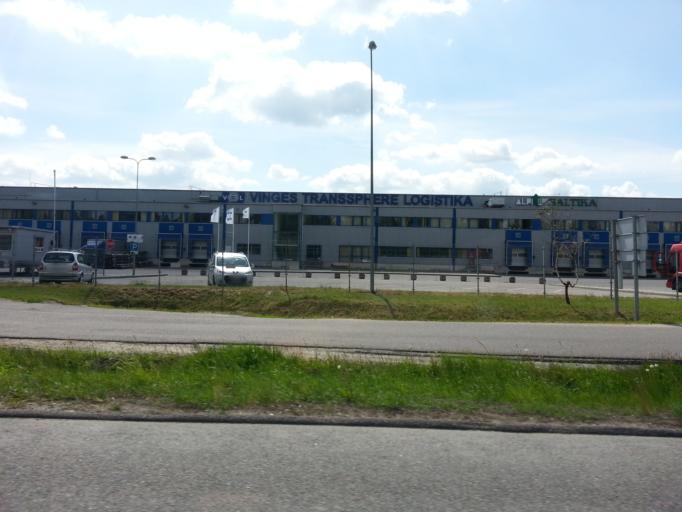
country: LT
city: Lentvaris
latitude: 54.7014
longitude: 25.0085
